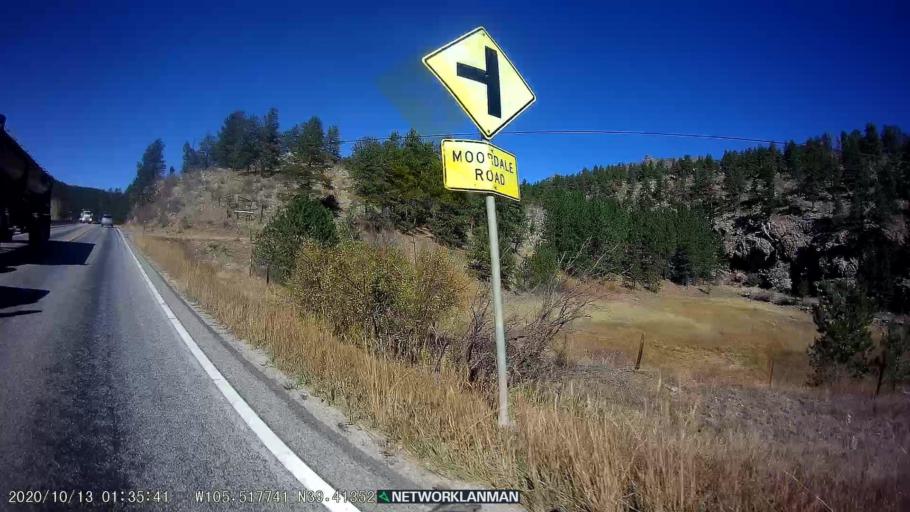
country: US
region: Colorado
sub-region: Jefferson County
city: Evergreen
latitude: 39.4136
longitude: -105.5182
